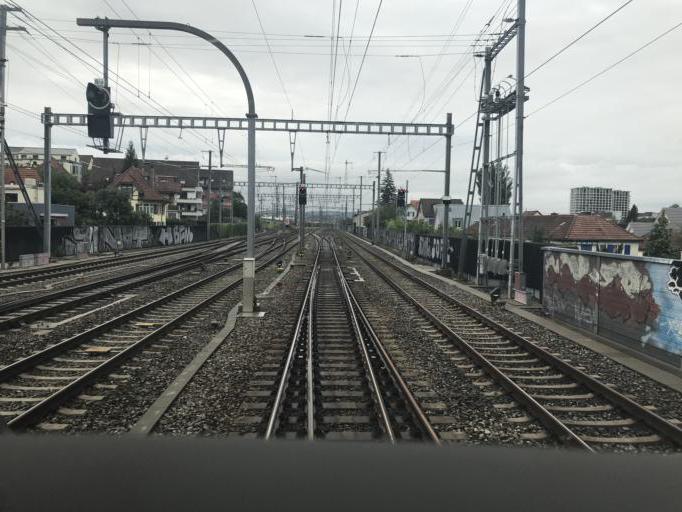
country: CH
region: Zurich
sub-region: Bezirk Zuerich
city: Zuerich (Kreis 11) / Seebach
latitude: 47.4151
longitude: 8.5487
